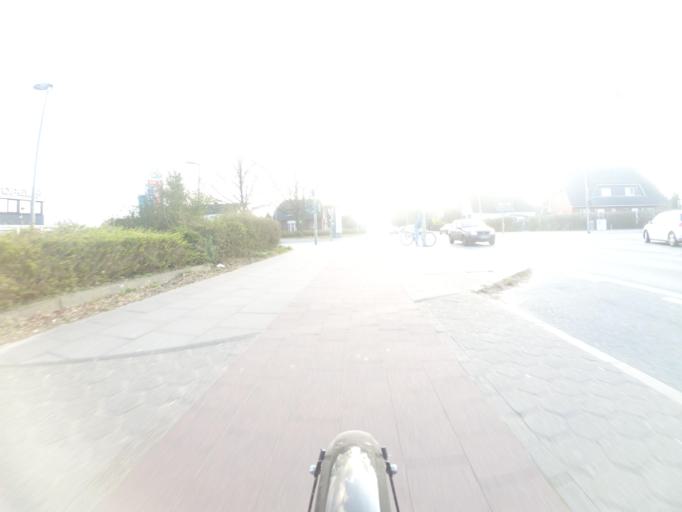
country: DE
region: Hamburg
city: Farmsen-Berne
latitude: 53.6238
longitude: 10.1115
